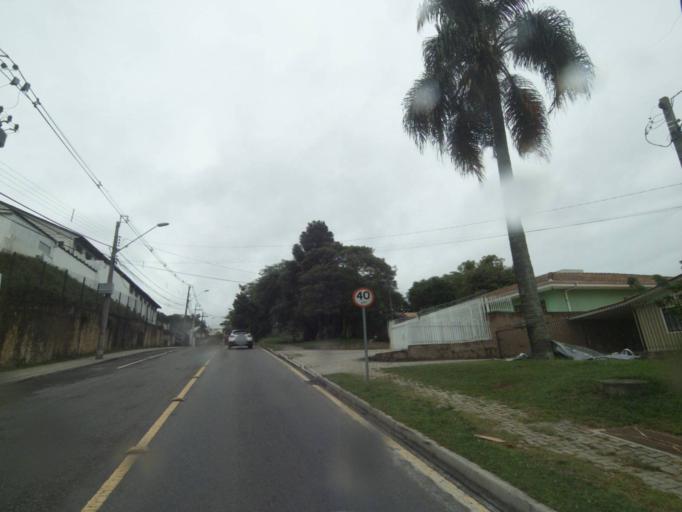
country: BR
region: Parana
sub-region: Curitiba
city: Curitiba
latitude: -25.4285
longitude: -49.3213
